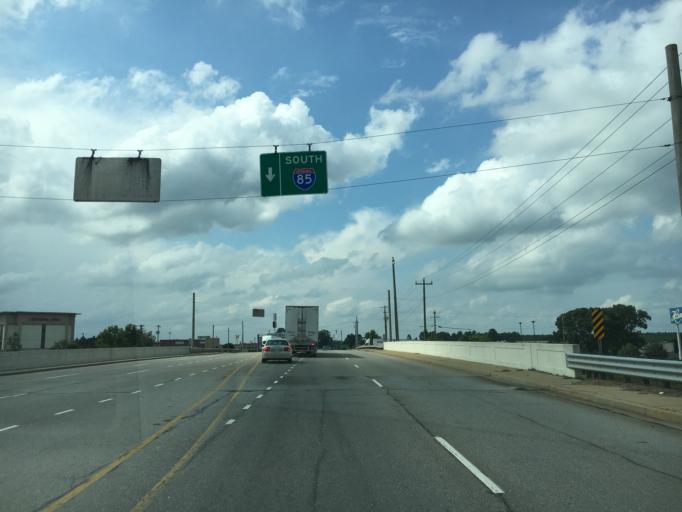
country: US
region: South Carolina
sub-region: Cherokee County
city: Gaffney
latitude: 35.0823
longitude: -81.7057
